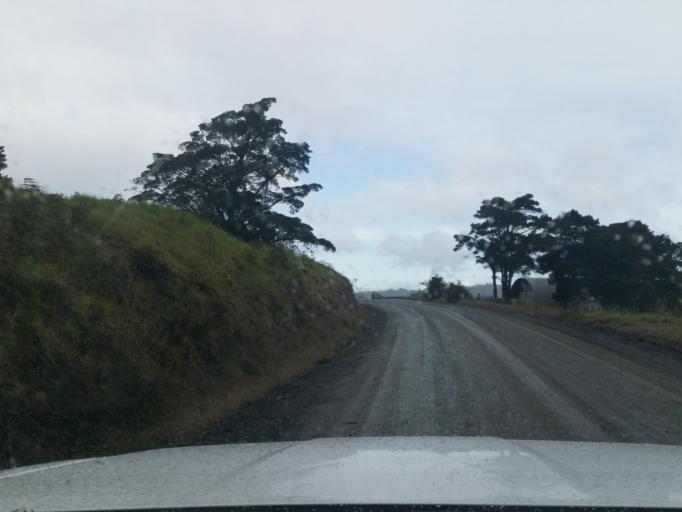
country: NZ
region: Northland
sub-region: Kaipara District
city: Dargaville
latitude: -35.8238
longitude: 173.7792
